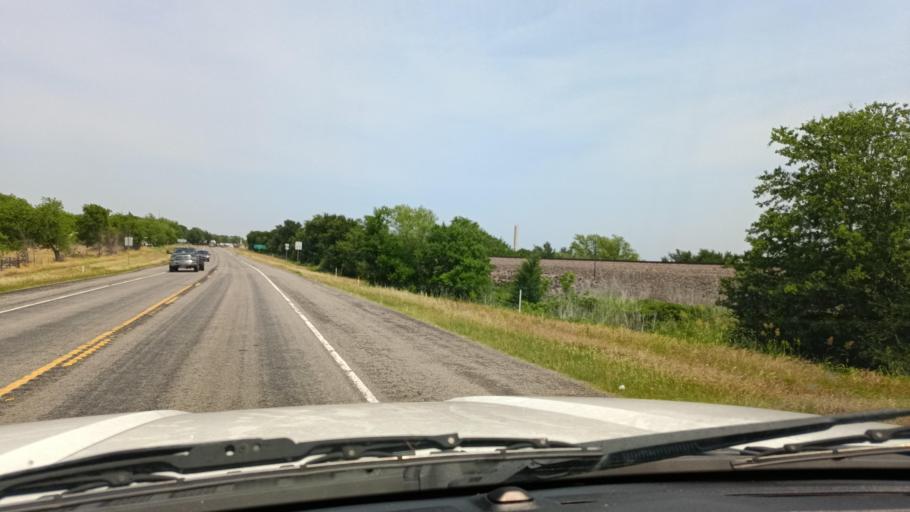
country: US
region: Texas
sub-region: Bell County
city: Rogers
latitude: 30.8757
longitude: -97.1334
